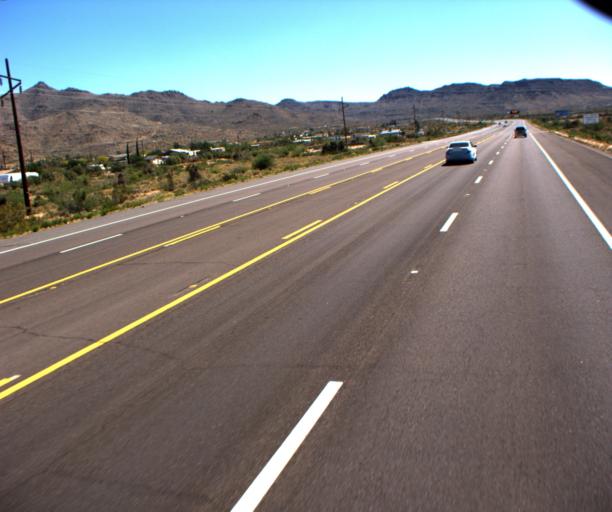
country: US
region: Arizona
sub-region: Mohave County
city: Golden Valley
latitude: 35.2187
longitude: -114.1493
